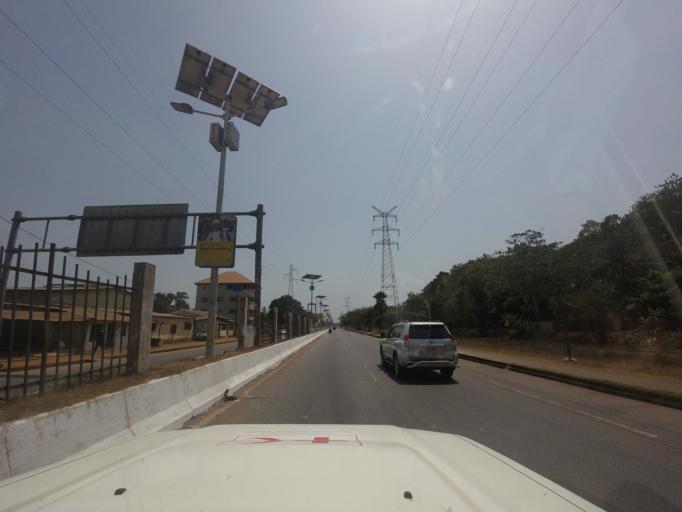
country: GN
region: Conakry
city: Camayenne
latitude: 9.5311
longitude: -13.6838
